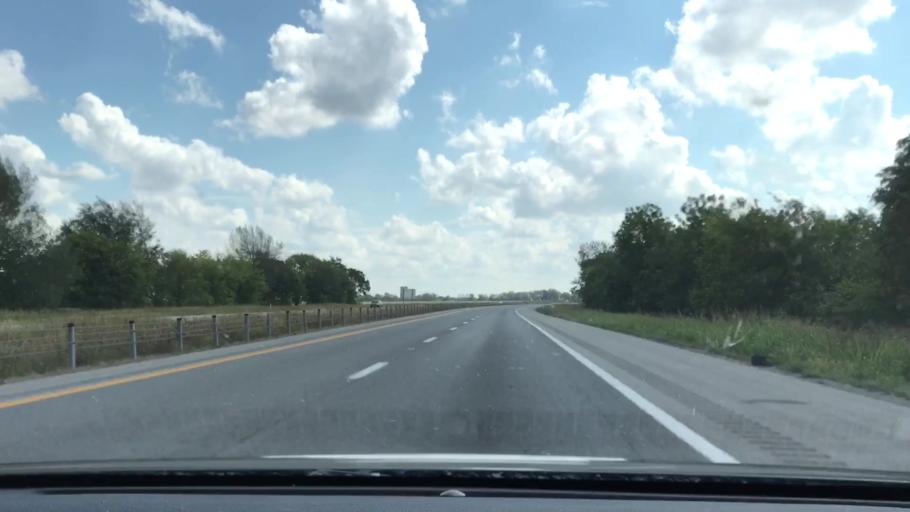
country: US
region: Kentucky
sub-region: Christian County
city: Oak Grove
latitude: 36.7353
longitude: -87.4966
